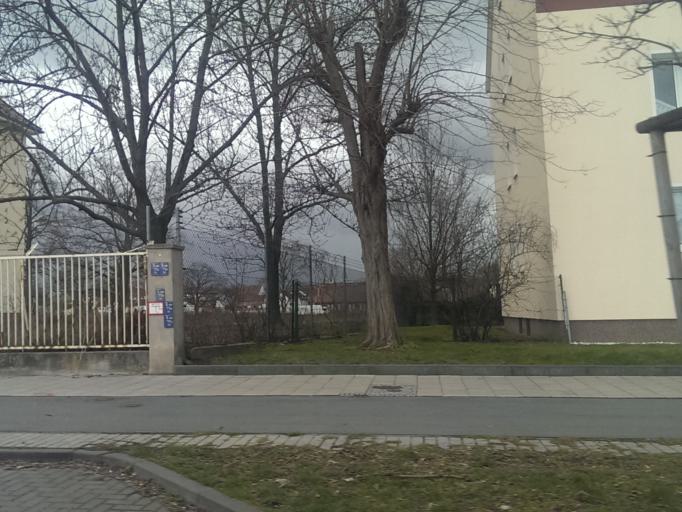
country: DE
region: Lower Saxony
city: Hildesheim
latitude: 52.1557
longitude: 9.9724
